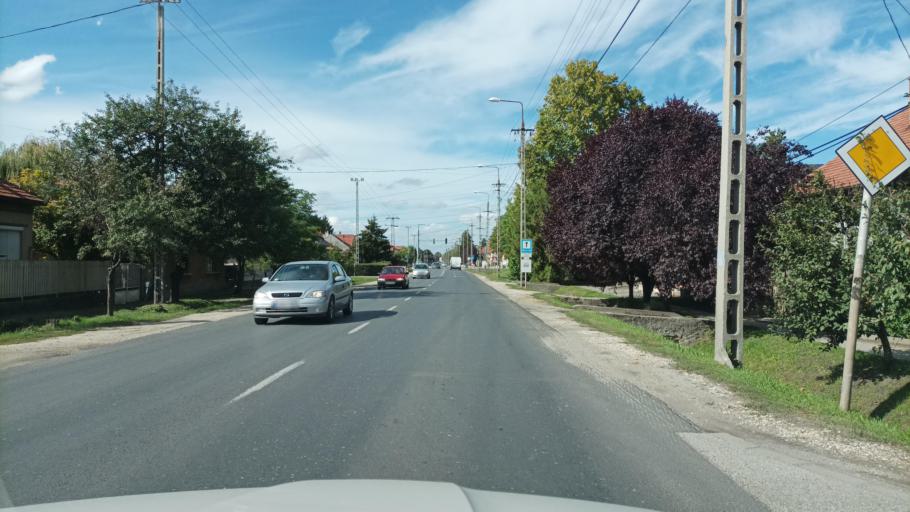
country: HU
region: Pest
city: Ullo
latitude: 47.3823
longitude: 19.3515
